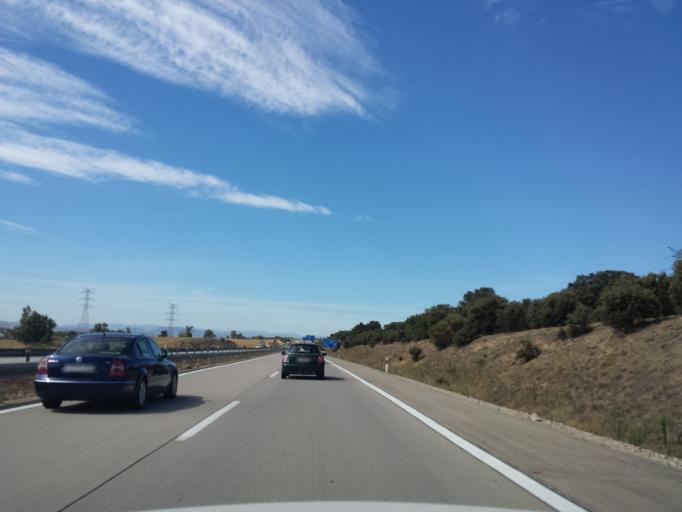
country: ES
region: Castille-La Mancha
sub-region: Province of Toledo
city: Mejorada
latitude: 39.9689
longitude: -4.8944
